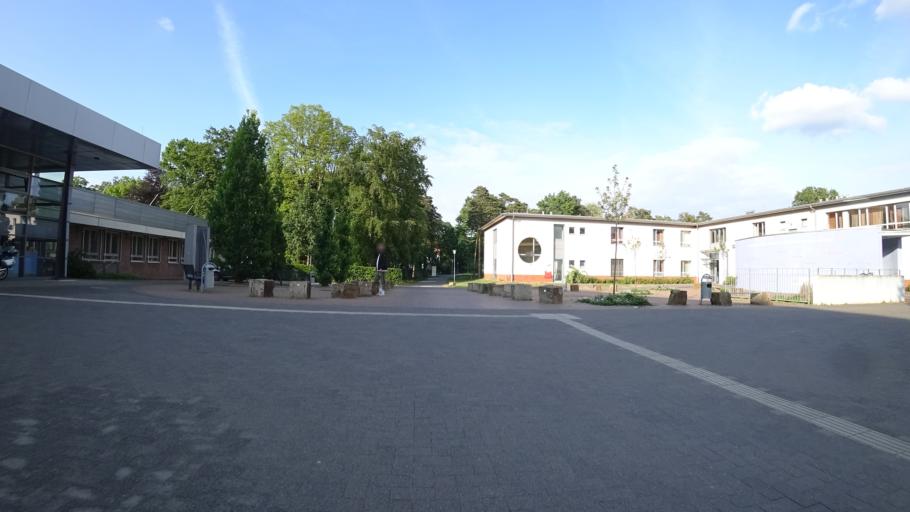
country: DE
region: North Rhine-Westphalia
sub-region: Regierungsbezirk Detmold
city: Guetersloh
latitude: 51.8944
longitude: 8.3518
